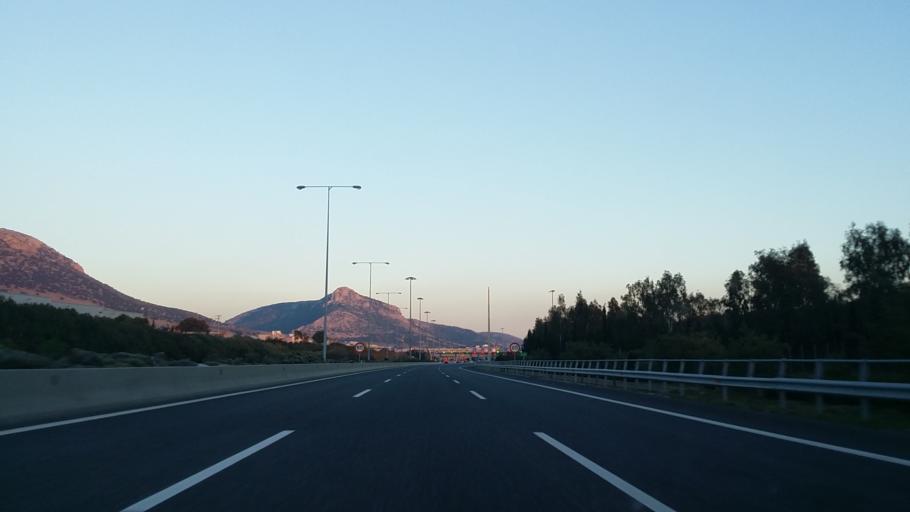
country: GR
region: Attica
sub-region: Nomarchia Dytikis Attikis
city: Aspropyrgos
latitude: 38.0945
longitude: 23.5848
